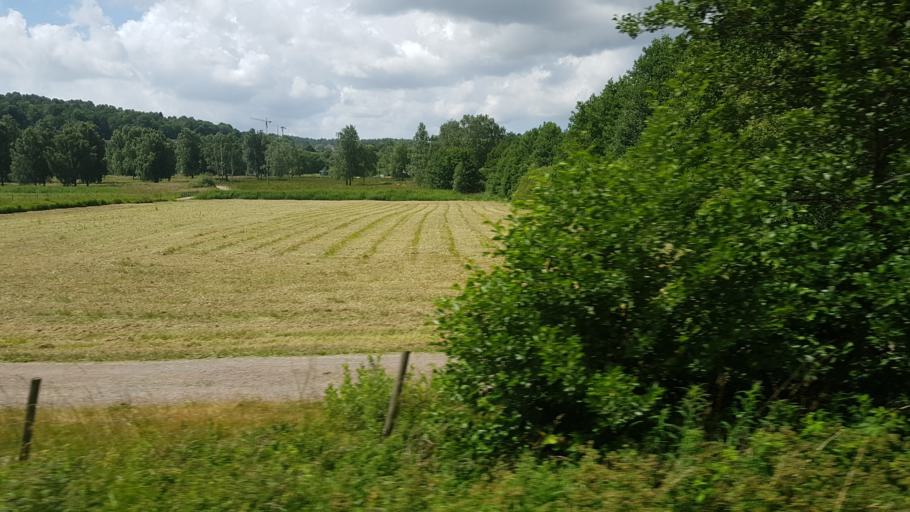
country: SE
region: Vaestra Goetaland
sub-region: Goteborg
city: Goeteborg
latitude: 57.7609
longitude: 11.9446
